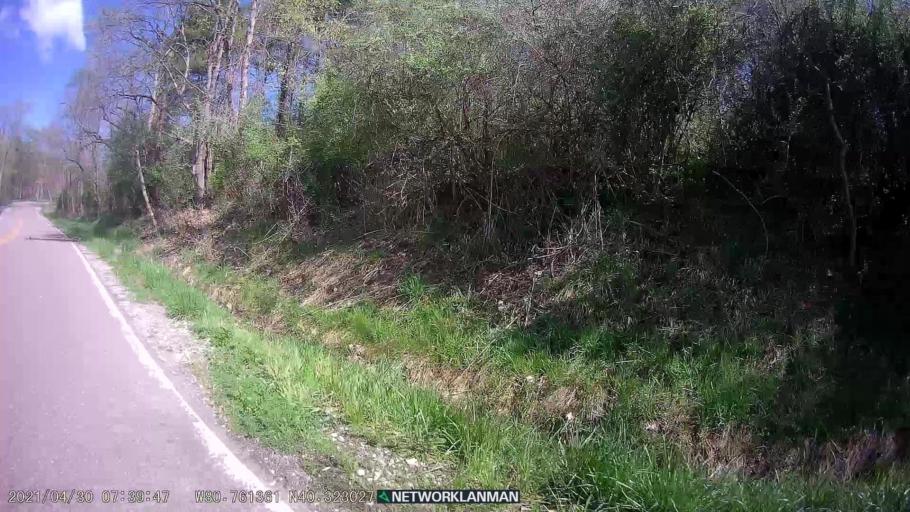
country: US
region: Ohio
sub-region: Jefferson County
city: Wintersville
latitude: 40.3230
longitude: -80.7614
